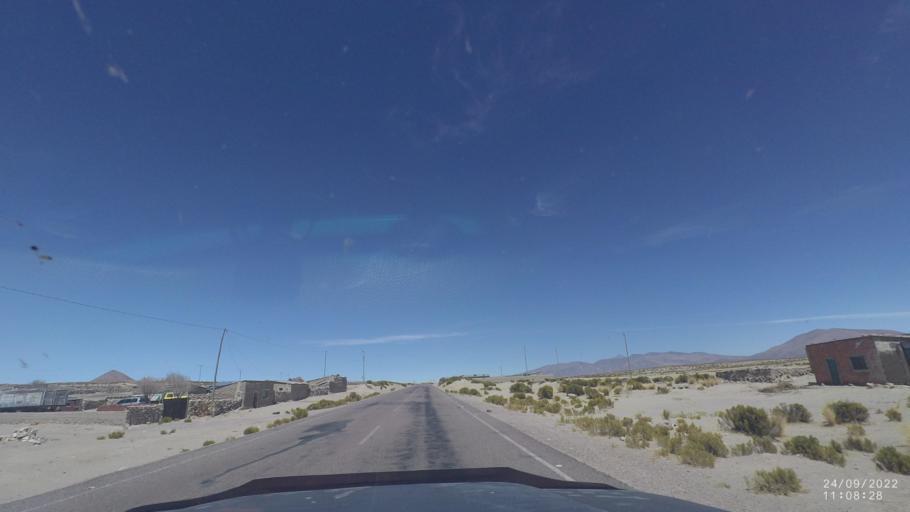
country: BO
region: Oruro
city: Challapata
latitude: -19.4854
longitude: -67.4421
